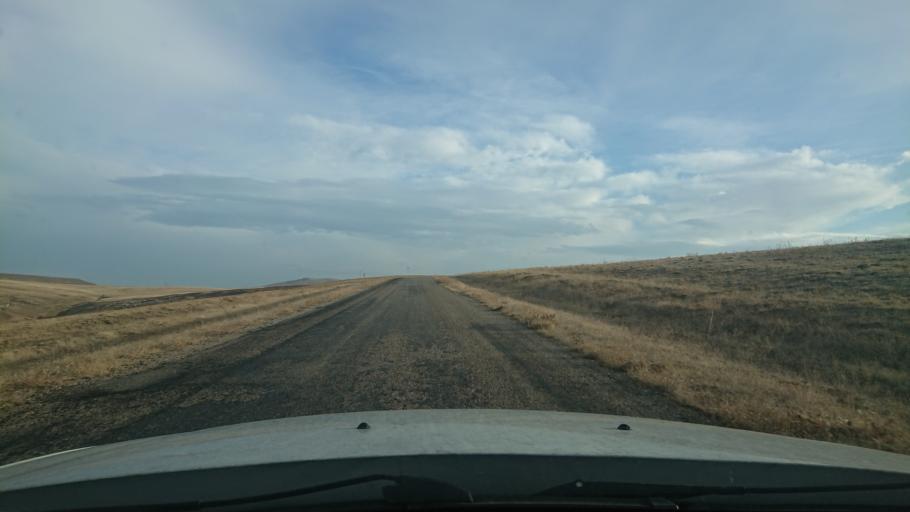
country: TR
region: Aksaray
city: Acipinar
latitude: 38.6584
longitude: 33.8384
